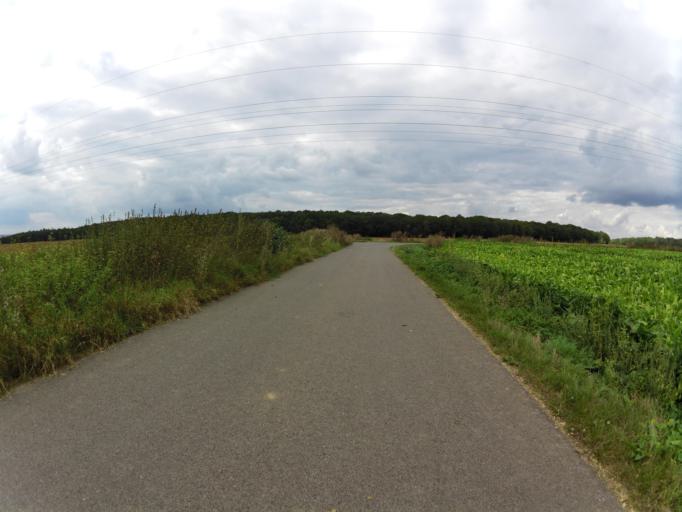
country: DE
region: Bavaria
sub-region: Regierungsbezirk Unterfranken
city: Rottendorf
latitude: 49.8051
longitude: 10.0237
